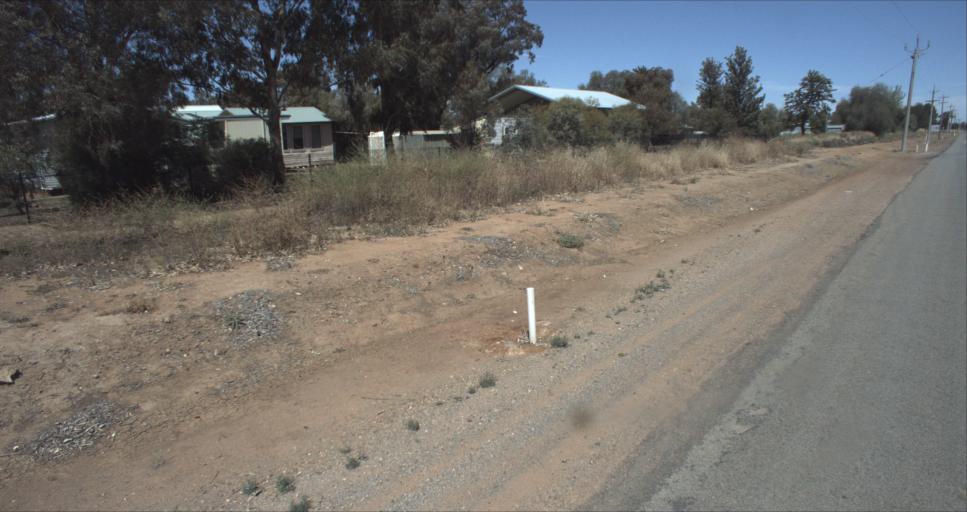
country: AU
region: New South Wales
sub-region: Leeton
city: Leeton
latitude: -34.5252
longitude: 146.3301
